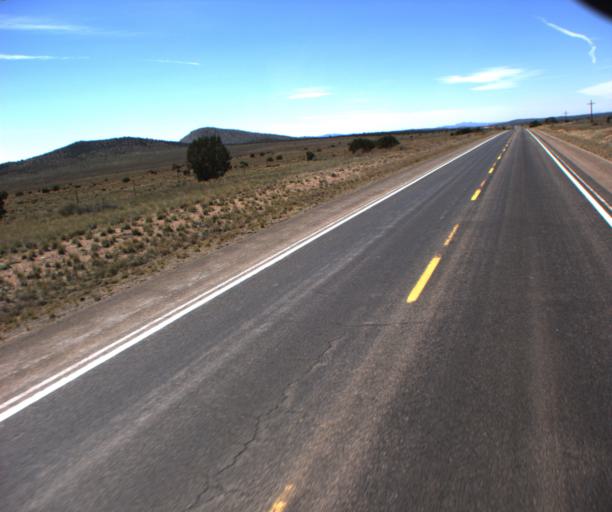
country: US
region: Arizona
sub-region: Mohave County
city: Peach Springs
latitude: 35.5401
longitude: -113.2677
